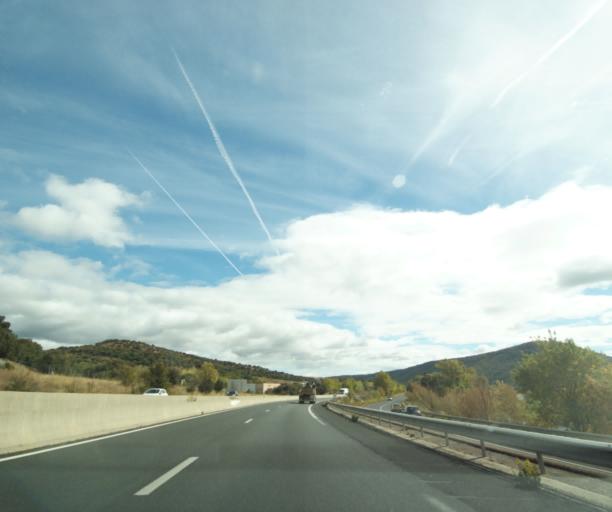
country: FR
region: Languedoc-Roussillon
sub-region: Departement de l'Herault
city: Lodeve
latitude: 43.6919
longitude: 3.3477
